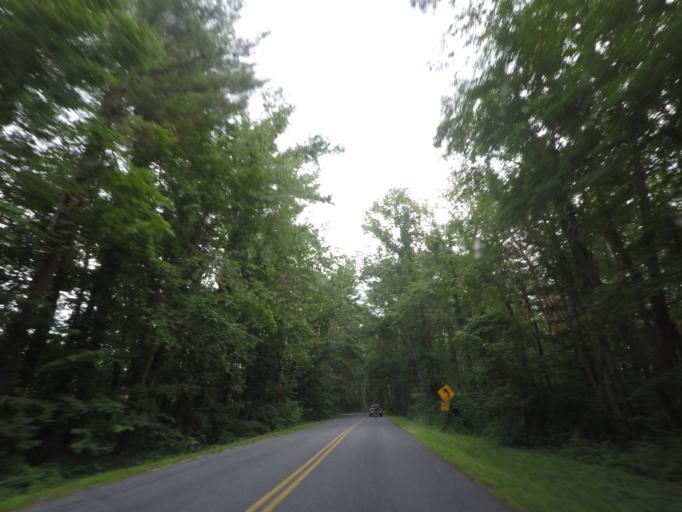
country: US
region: New York
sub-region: Rensselaer County
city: Poestenkill
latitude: 42.8401
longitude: -73.5313
